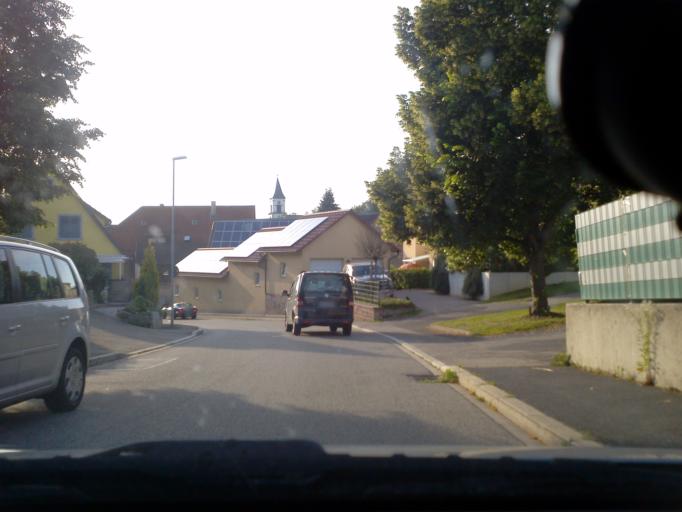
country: DE
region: Baden-Wuerttemberg
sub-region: Karlsruhe Region
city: Woessingen
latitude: 49.0094
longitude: 8.6142
